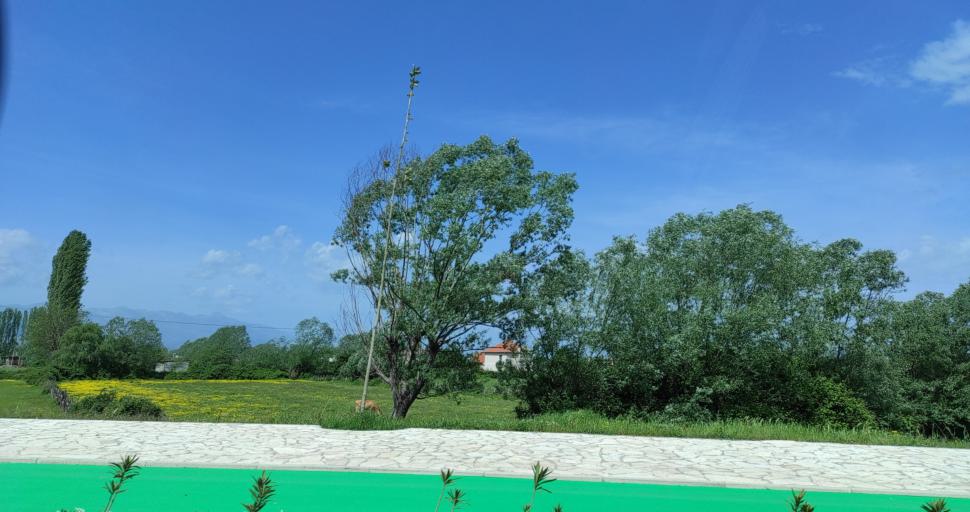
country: AL
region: Shkoder
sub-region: Rrethi i Shkodres
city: Shkoder
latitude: 42.0812
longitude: 19.4928
